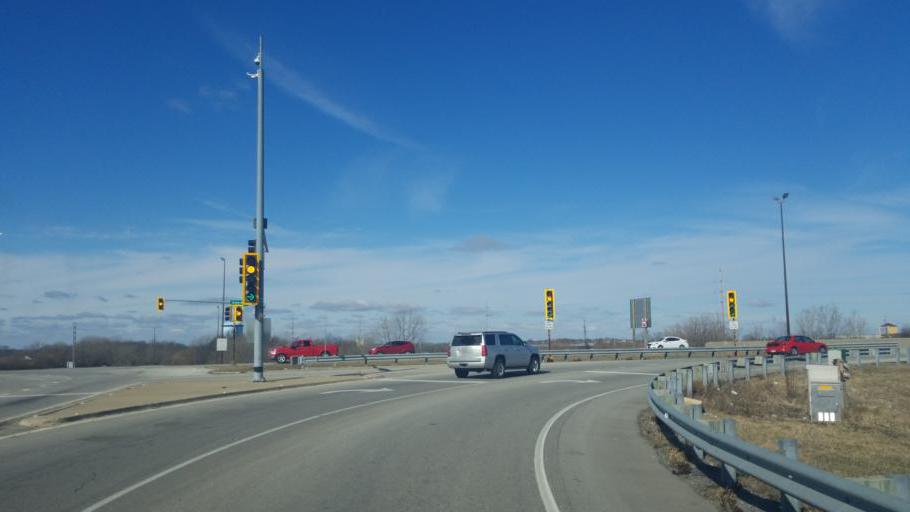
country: US
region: Illinois
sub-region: Sangamon County
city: Jerome
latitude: 39.7452
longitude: -89.7054
